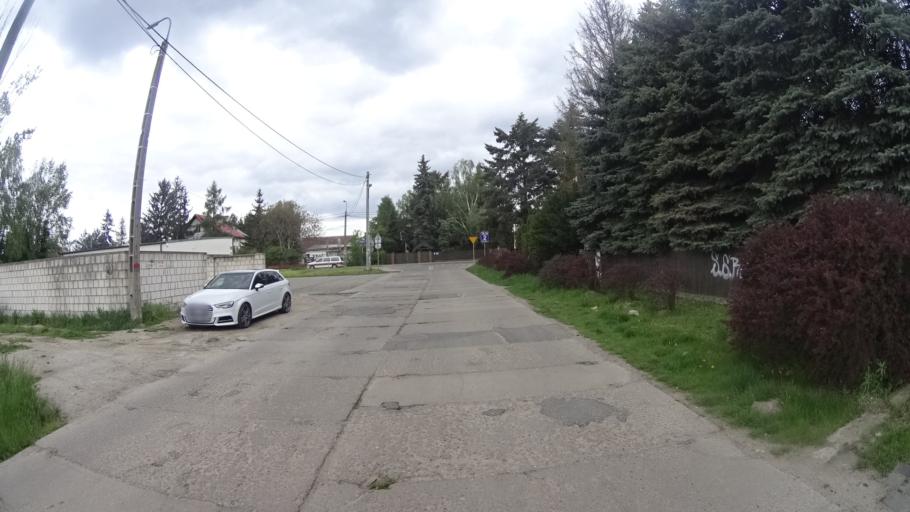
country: PL
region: Masovian Voivodeship
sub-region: Warszawa
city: Bemowo
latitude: 52.2853
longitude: 20.8874
